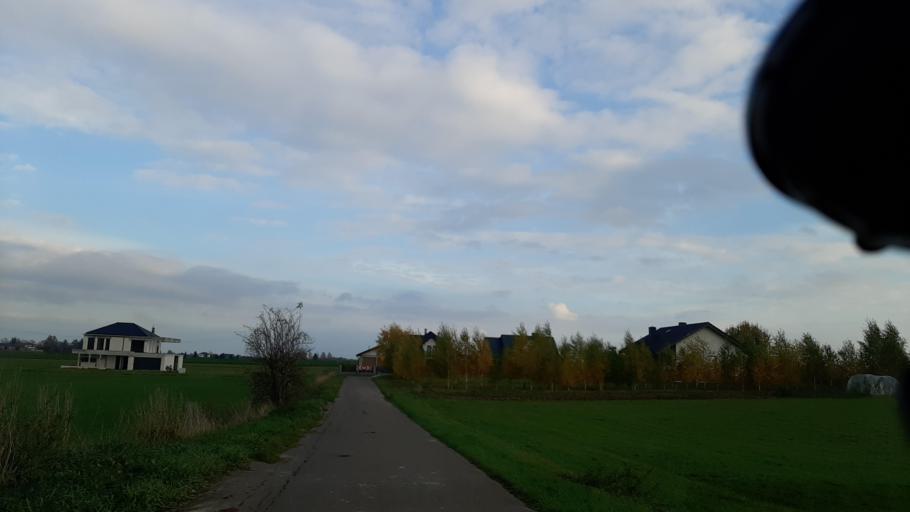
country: PL
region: Lublin Voivodeship
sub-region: Powiat lubelski
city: Garbow
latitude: 51.3378
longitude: 22.3225
